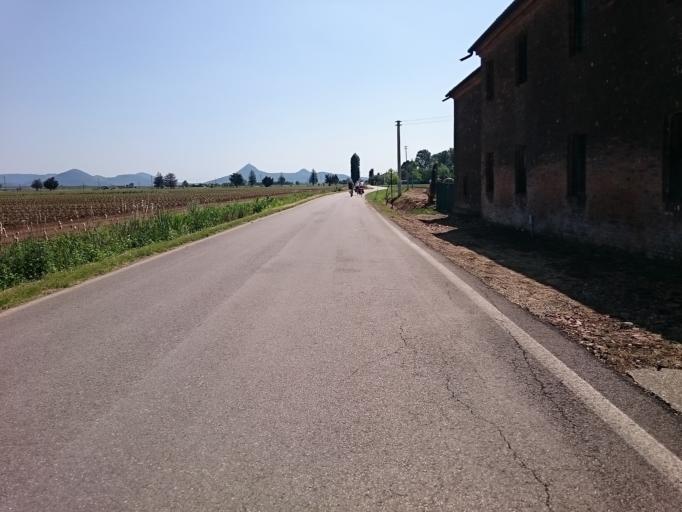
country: IT
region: Veneto
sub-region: Provincia di Padova
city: Saletto
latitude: 45.2524
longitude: 11.5470
